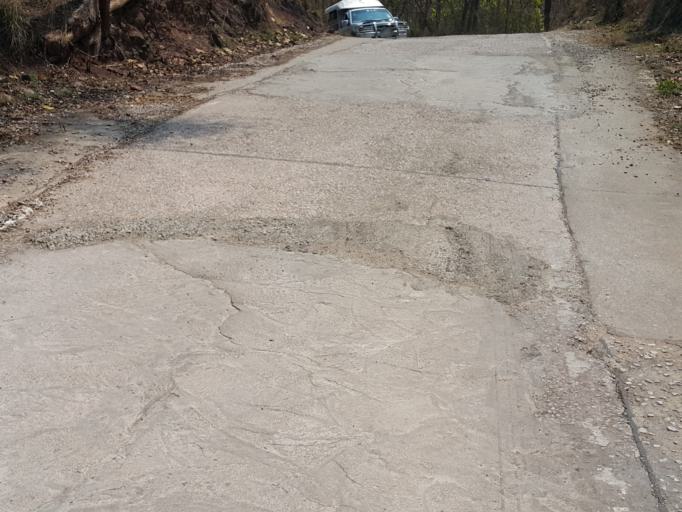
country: TH
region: Lampang
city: Chae Hom
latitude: 18.7461
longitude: 99.5414
